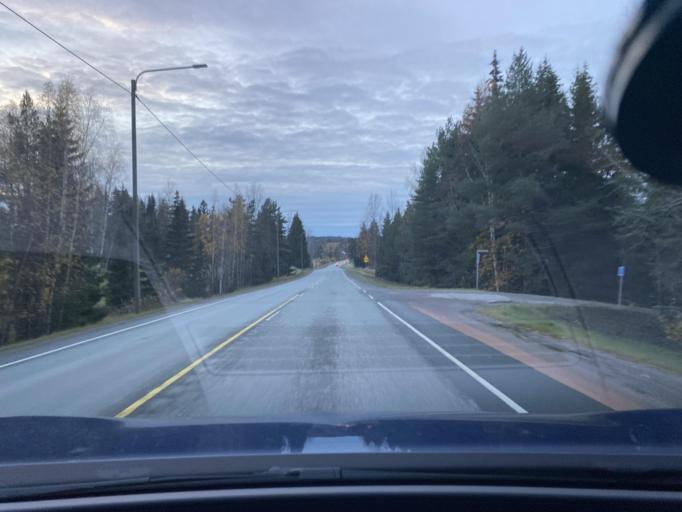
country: FI
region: Uusimaa
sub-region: Helsinki
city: Lohja
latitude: 60.3714
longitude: 24.1172
